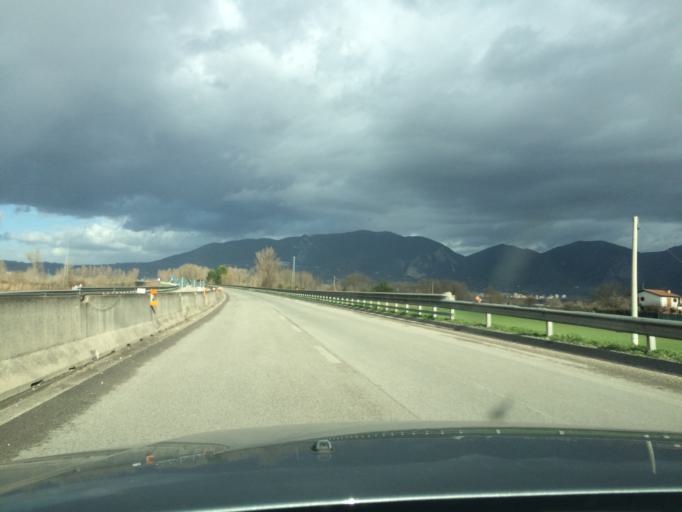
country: IT
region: Umbria
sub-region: Provincia di Terni
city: Terni
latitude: 42.5529
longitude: 12.5839
